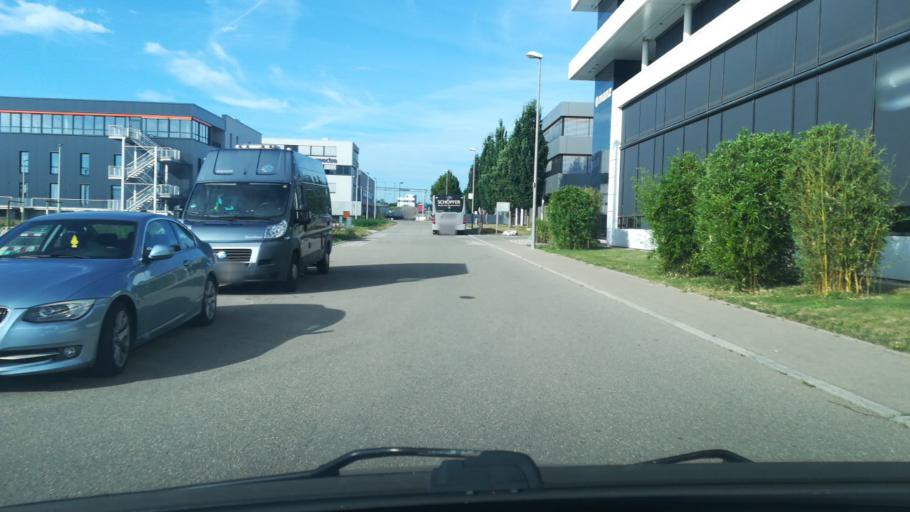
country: DE
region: Baden-Wuerttemberg
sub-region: Tuebingen Region
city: Sickenhausen
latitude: 48.5436
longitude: 9.1722
